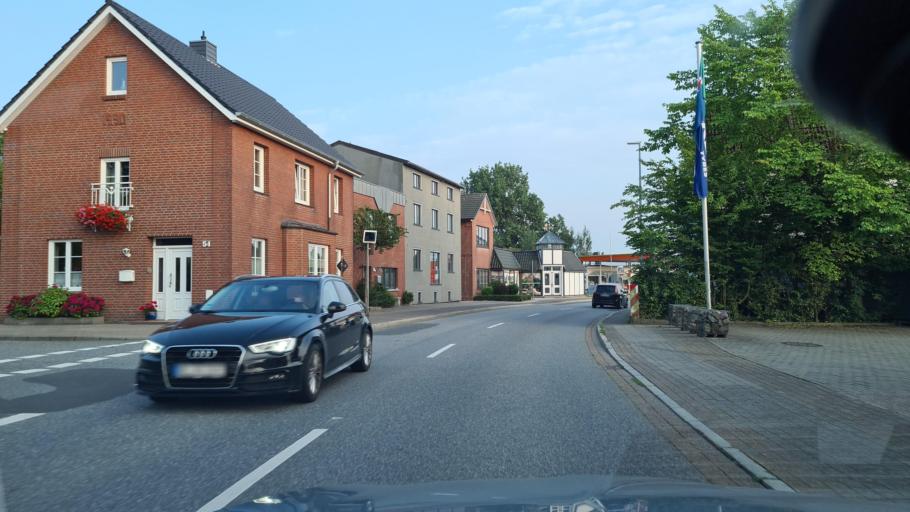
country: DE
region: Schleswig-Holstein
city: Husum
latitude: 54.4675
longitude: 9.0539
